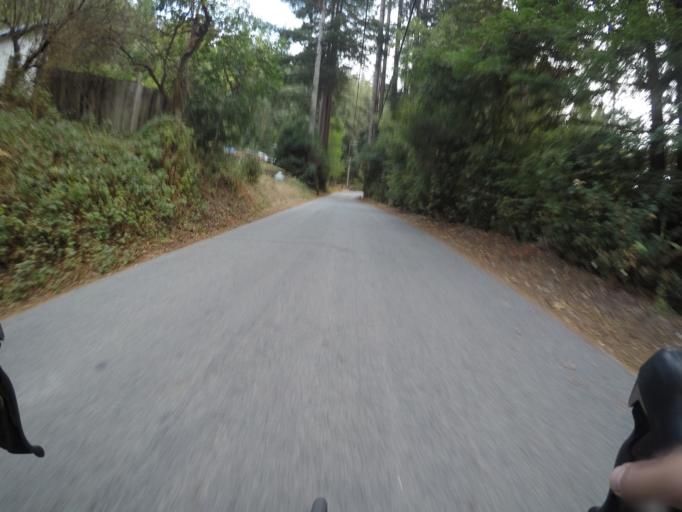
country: US
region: California
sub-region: Santa Cruz County
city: Scotts Valley
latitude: 37.0640
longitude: -122.0178
